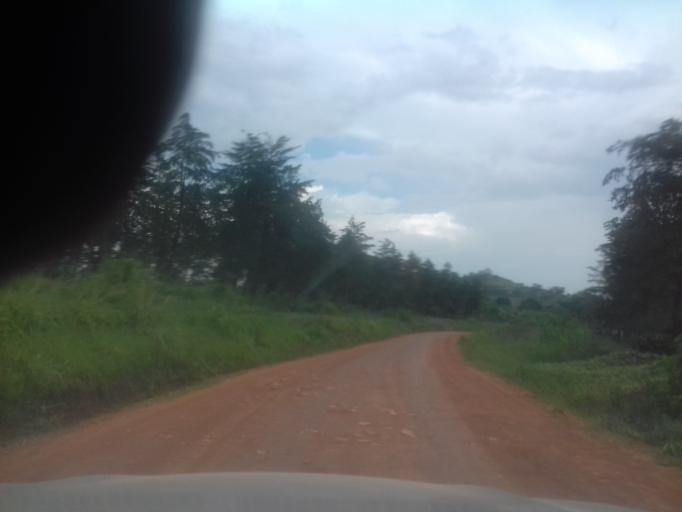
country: UG
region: Northern Region
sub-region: Zombo District
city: Paidha
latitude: 2.2524
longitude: 30.8677
